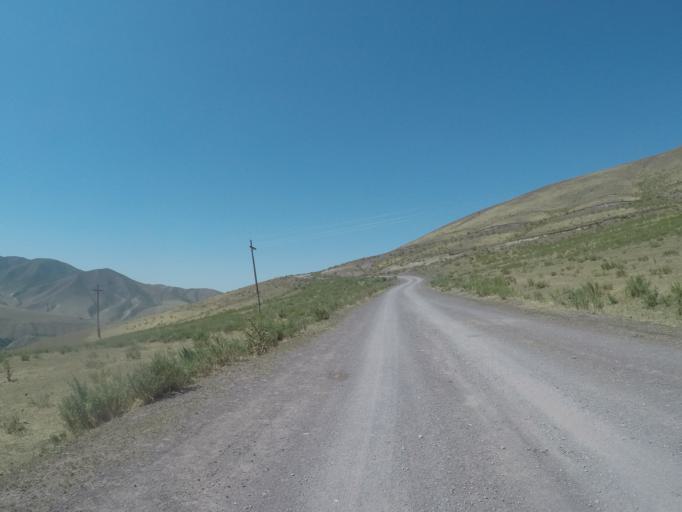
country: KG
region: Chuy
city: Bishkek
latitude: 42.6499
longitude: 74.5172
